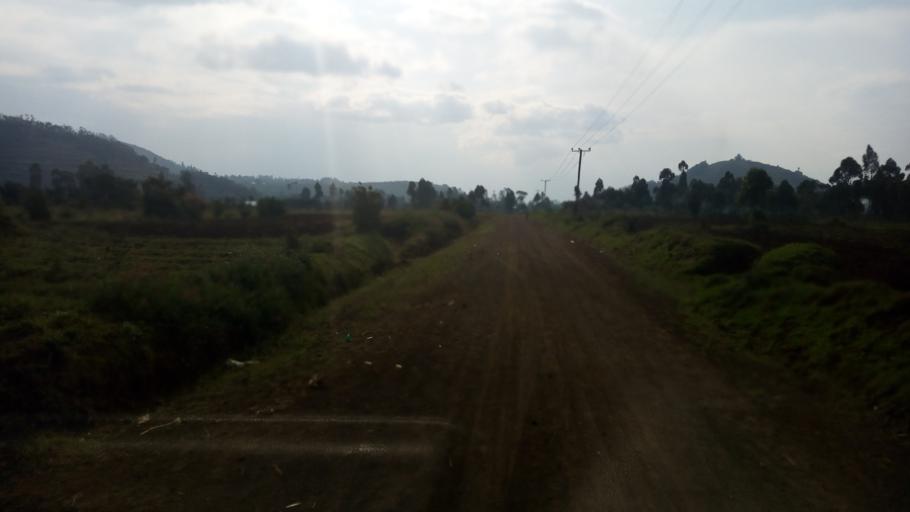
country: UG
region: Western Region
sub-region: Kisoro District
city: Kisoro
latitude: -1.3083
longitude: 29.7153
